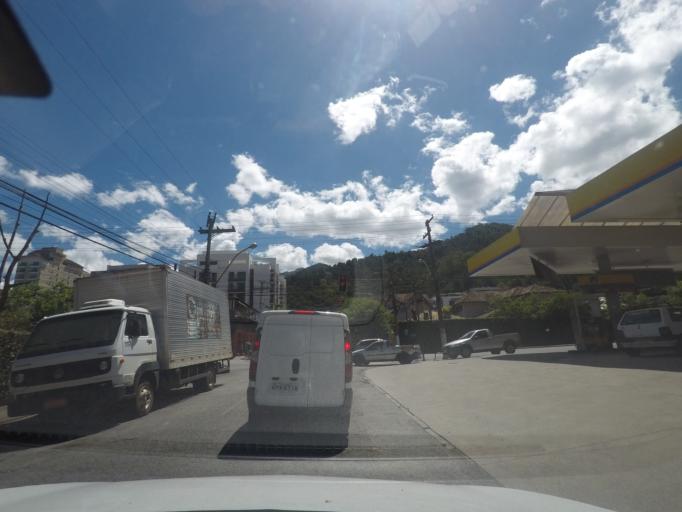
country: BR
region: Rio de Janeiro
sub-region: Teresopolis
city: Teresopolis
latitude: -22.4299
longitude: -42.9794
